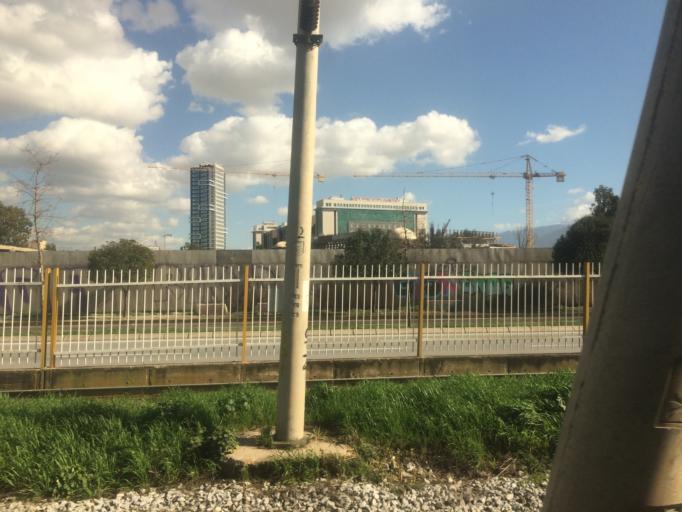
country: TR
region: Izmir
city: Buca
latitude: 38.4436
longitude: 27.1737
